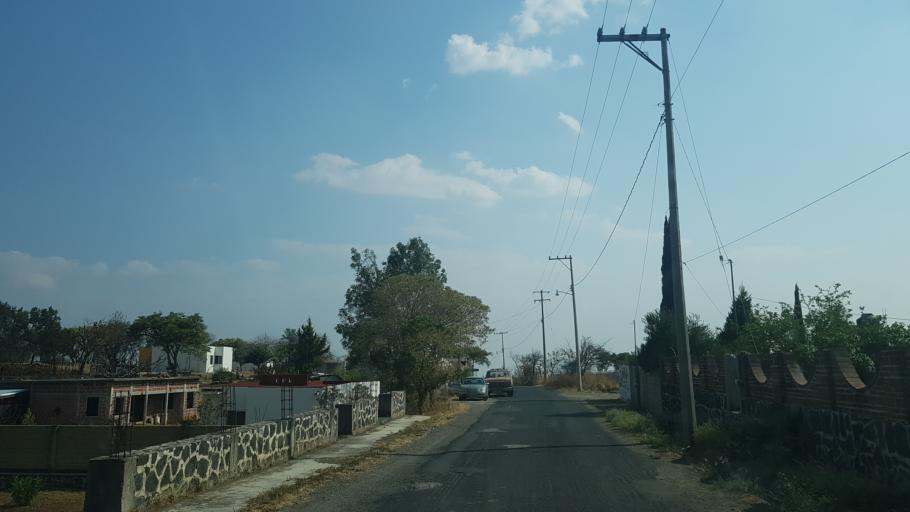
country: MX
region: Morelos
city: Tlacotepec
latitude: 18.8077
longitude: -98.7132
